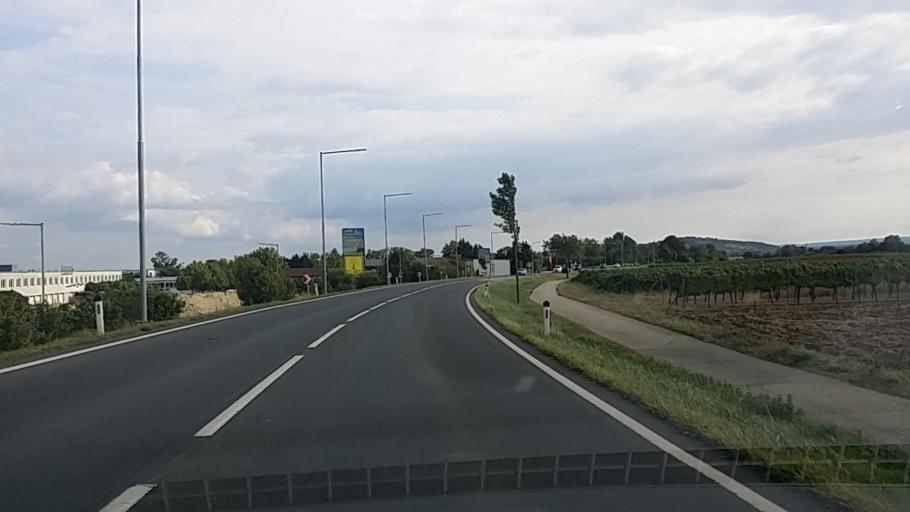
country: AT
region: Burgenland
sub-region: Eisenstadt-Umgebung
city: Donnerskirchen
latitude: 47.8766
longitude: 16.6494
